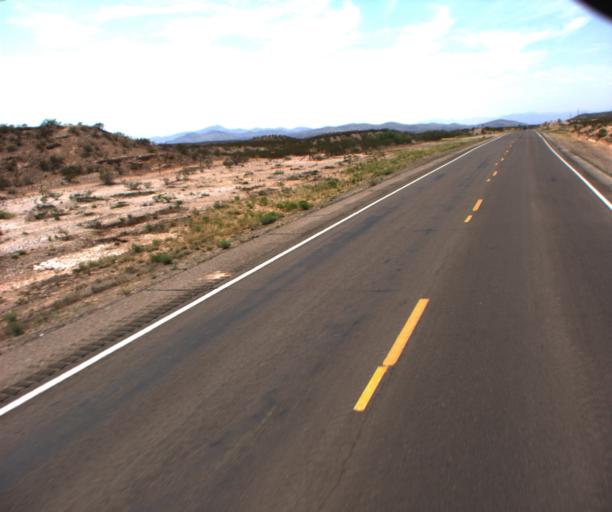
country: US
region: Arizona
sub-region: Greenlee County
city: Clifton
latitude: 32.7742
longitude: -109.1545
